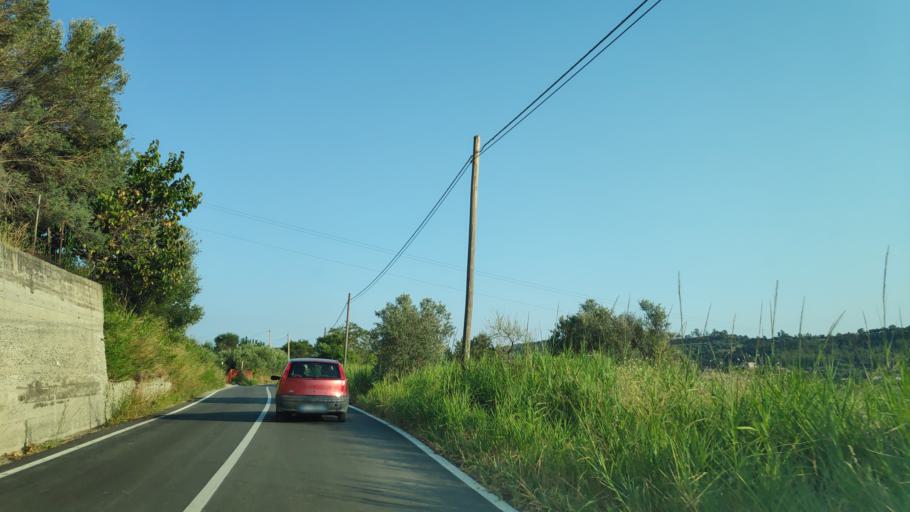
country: IT
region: Calabria
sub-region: Provincia di Reggio Calabria
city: Caulonia Marina
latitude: 38.3710
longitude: 16.4460
